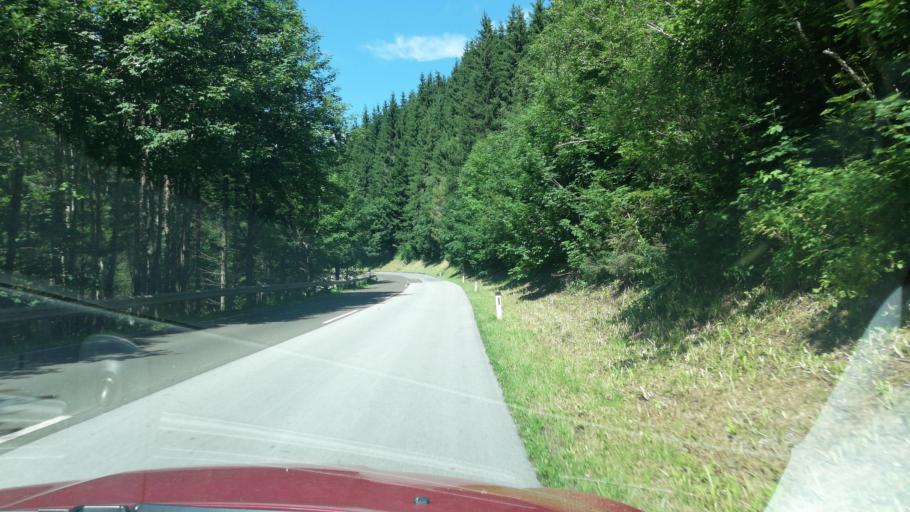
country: AT
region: Styria
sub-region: Politischer Bezirk Murtal
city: Hohentauern
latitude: 47.4477
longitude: 14.5062
